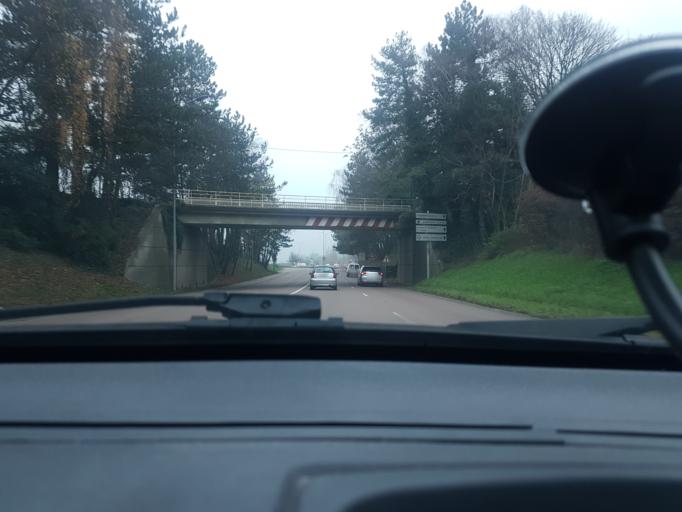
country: FR
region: Bourgogne
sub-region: Departement de Saone-et-Loire
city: Chalon-sur-Saone
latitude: 46.7941
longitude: 4.8390
